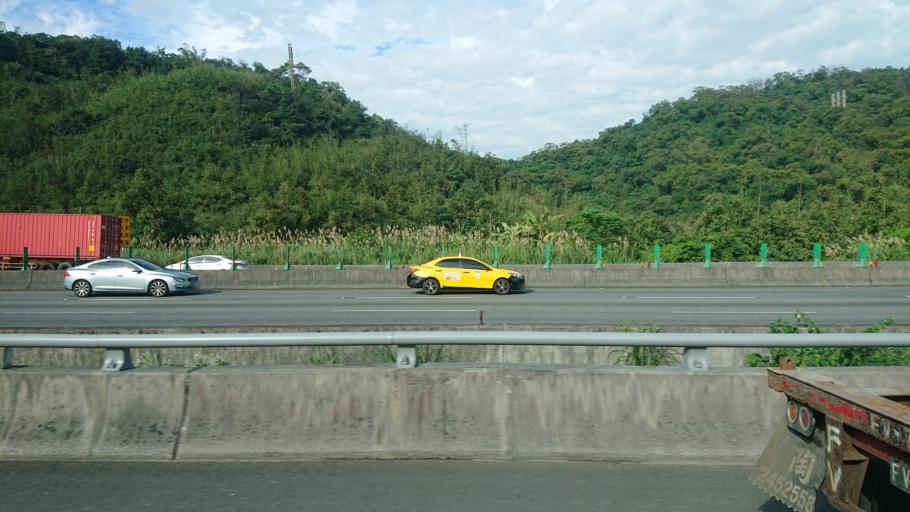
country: TW
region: Taiwan
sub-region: Keelung
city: Keelung
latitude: 25.0920
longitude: 121.6966
